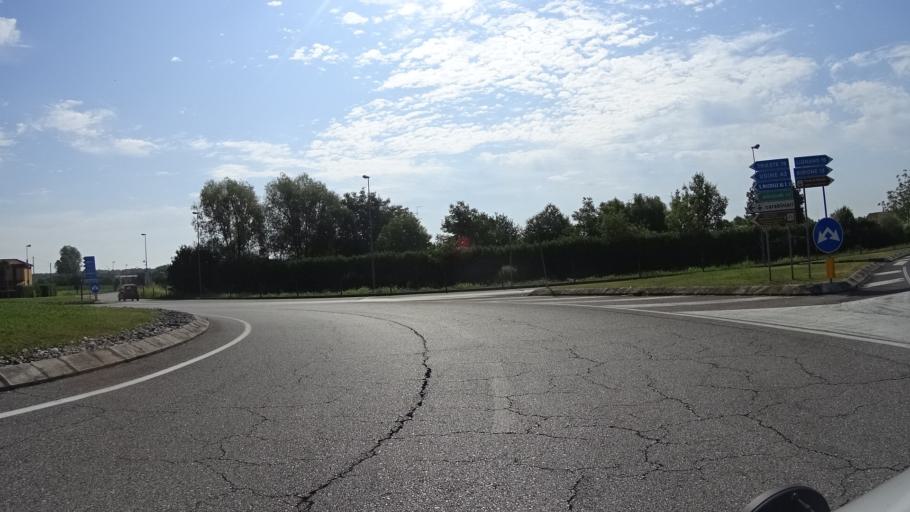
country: IT
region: Veneto
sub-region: Provincia di Venezia
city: San Michele al Tagliamento
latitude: 45.7479
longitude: 12.9900
